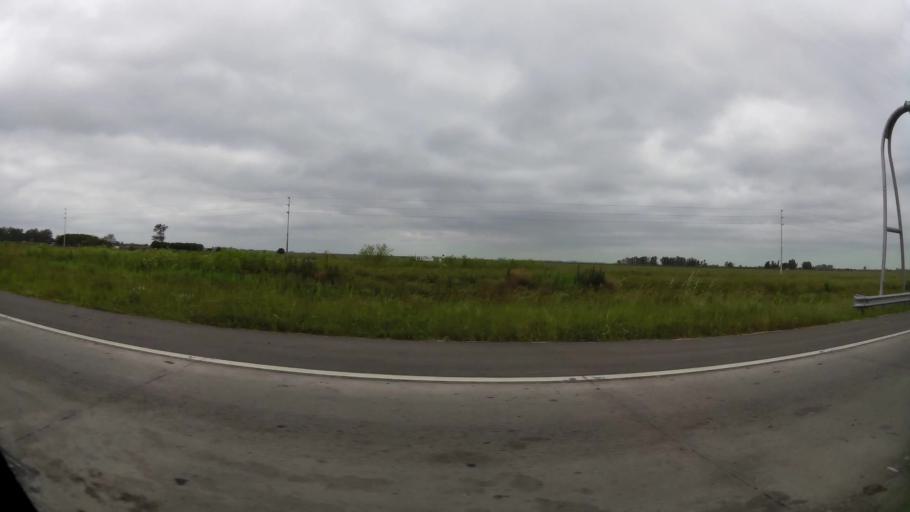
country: AR
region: Buenos Aires
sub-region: Partido de San Vicente
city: San Vicente
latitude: -35.0271
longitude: -58.3528
